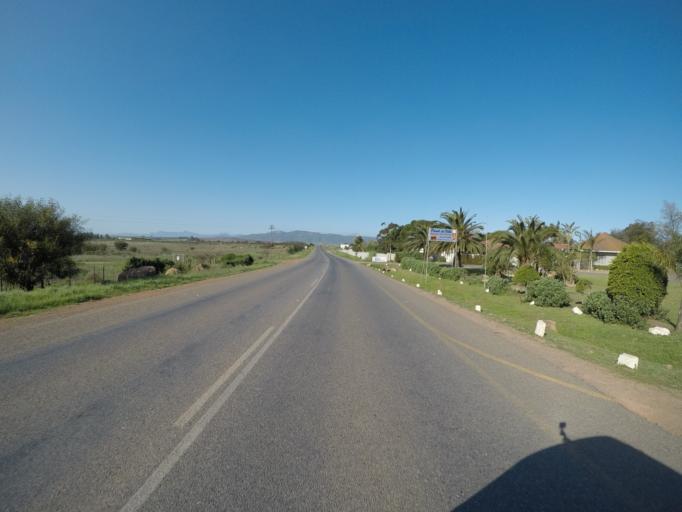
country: ZA
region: Western Cape
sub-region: City of Cape Town
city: Kraaifontein
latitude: -33.7664
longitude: 18.7879
